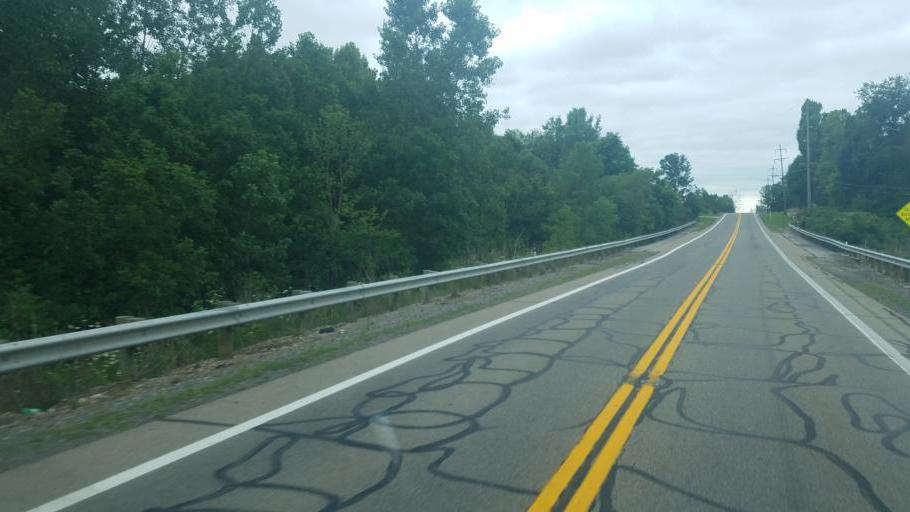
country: US
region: Ohio
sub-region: Pickaway County
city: Commercial Point
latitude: 39.7464
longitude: -83.0241
